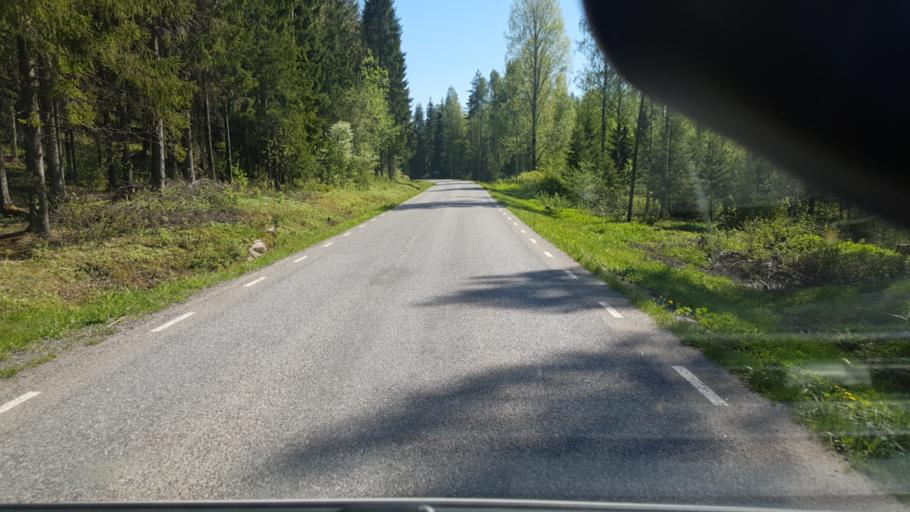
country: SE
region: Vaermland
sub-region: Eda Kommun
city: Amotfors
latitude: 59.8301
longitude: 12.4371
